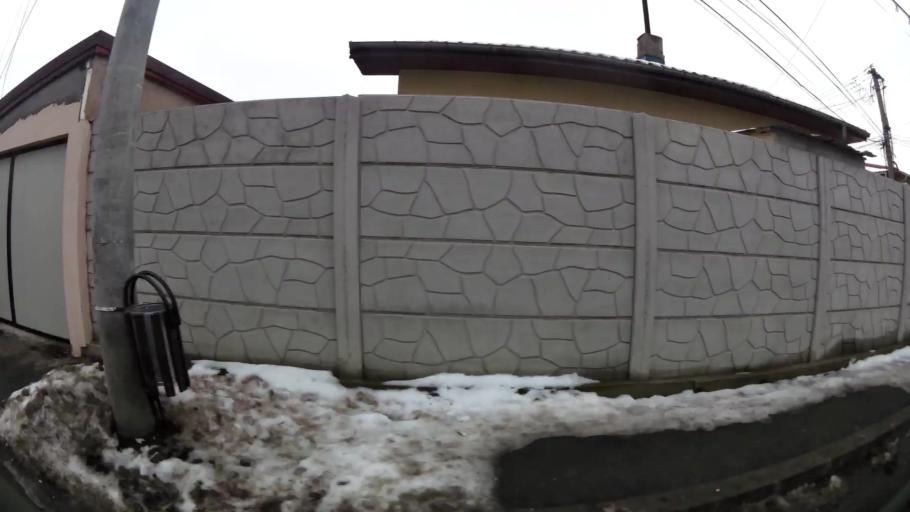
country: RO
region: Ilfov
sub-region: Comuna Pantelimon
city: Pantelimon
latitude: 44.4575
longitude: 26.2031
